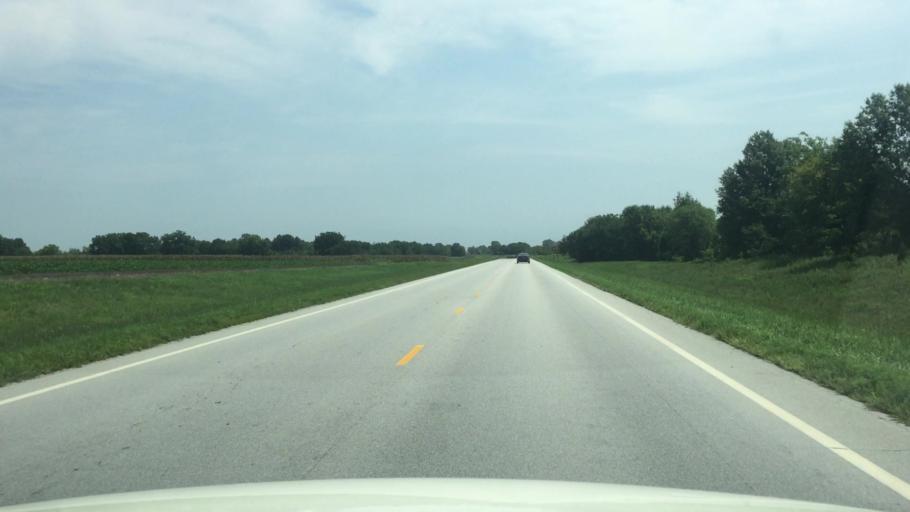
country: US
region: Kansas
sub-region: Cherokee County
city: Columbus
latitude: 37.1797
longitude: -94.9653
